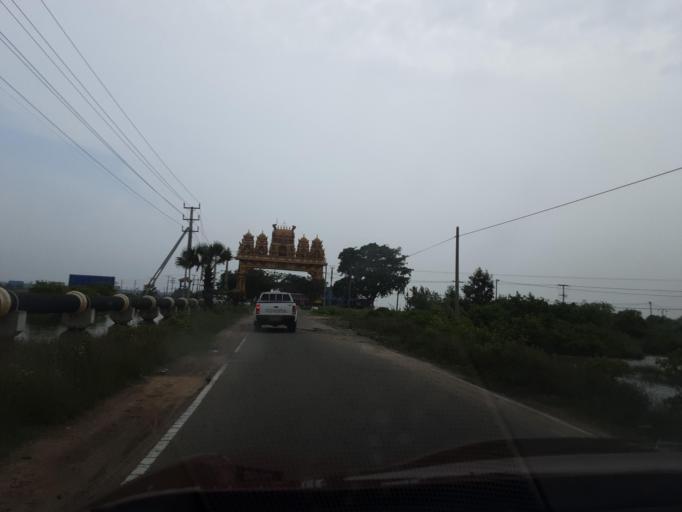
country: LK
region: Northern Province
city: Jaffna
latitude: 9.6633
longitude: 80.0610
